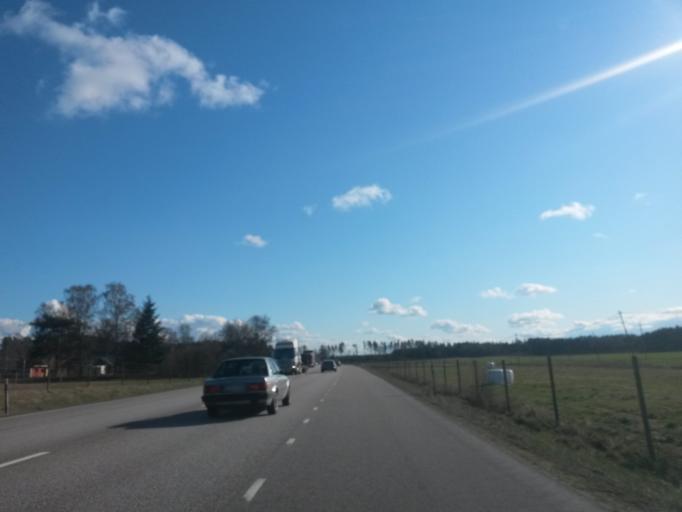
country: SE
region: Vaestra Goetaland
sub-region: Vara Kommun
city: Vara
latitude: 58.2020
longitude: 12.8984
